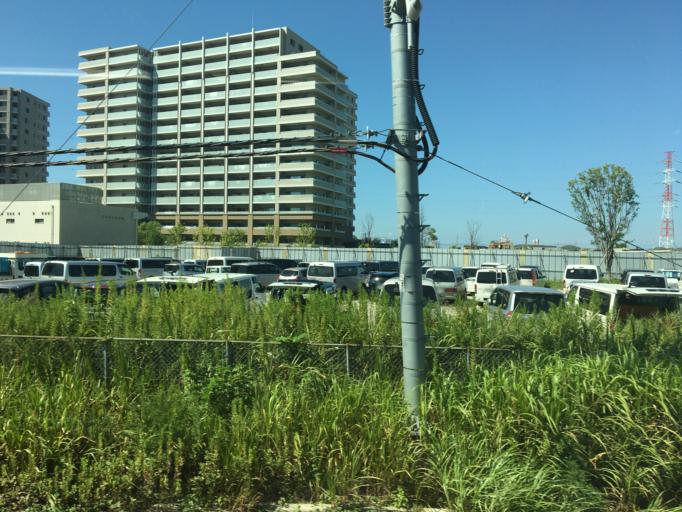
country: JP
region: Kanagawa
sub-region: Kawasaki-shi
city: Kawasaki
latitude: 35.5398
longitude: 139.6755
